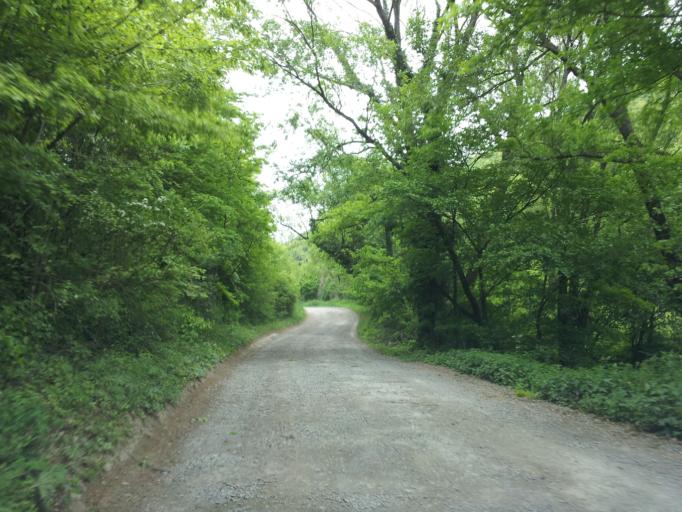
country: HU
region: Baranya
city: Hosszuheteny
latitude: 46.1763
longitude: 18.3485
